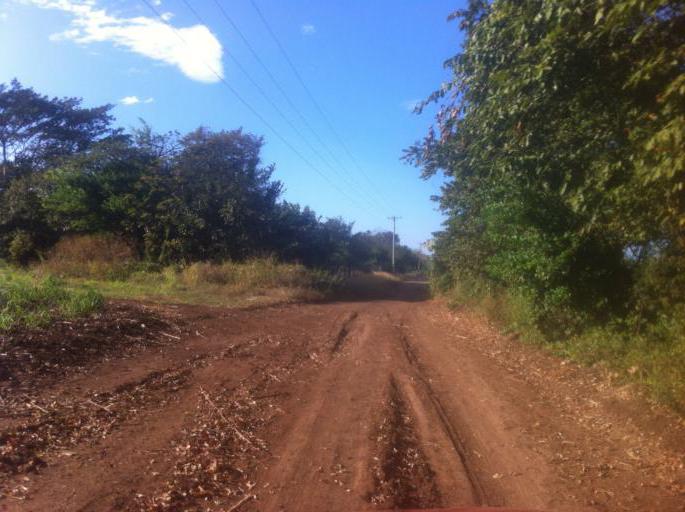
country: NI
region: Managua
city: Masachapa
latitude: 11.8695
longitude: -86.5645
